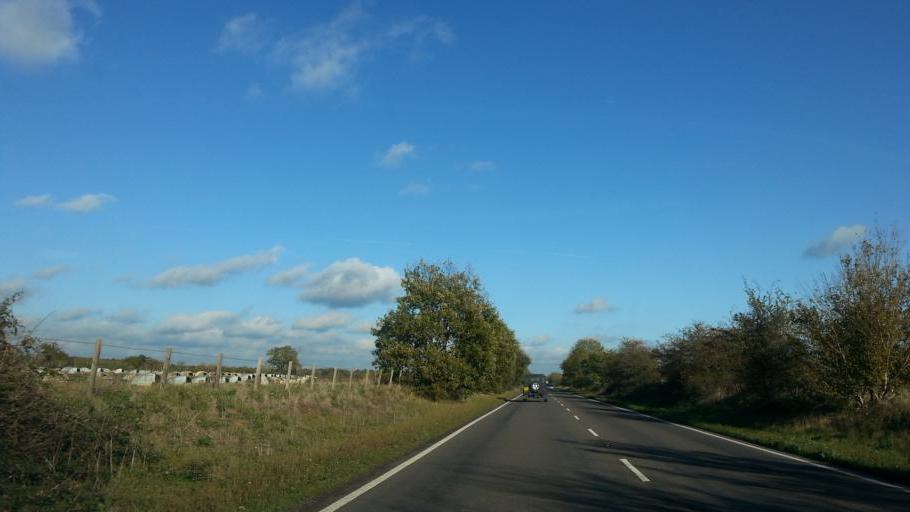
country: GB
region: England
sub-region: Suffolk
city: Bungay
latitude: 52.4439
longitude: 1.4011
